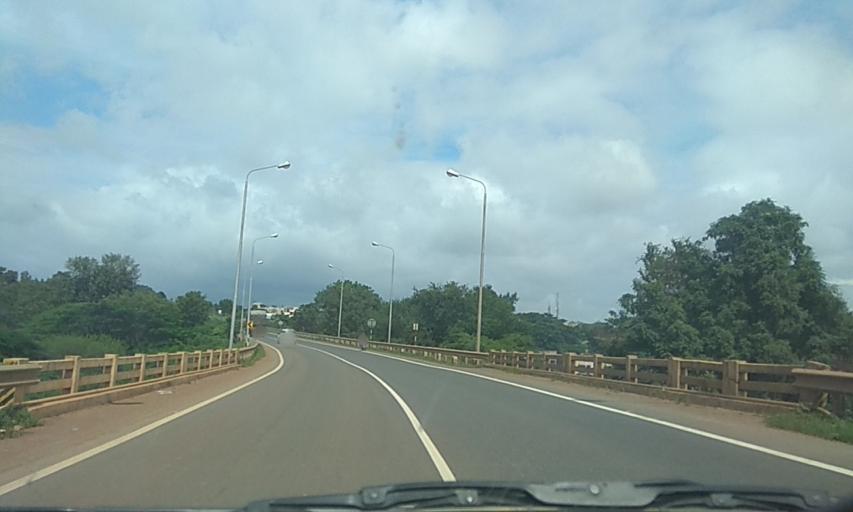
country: IN
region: Karnataka
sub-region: Dharwad
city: Hubli
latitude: 15.3291
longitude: 75.1191
